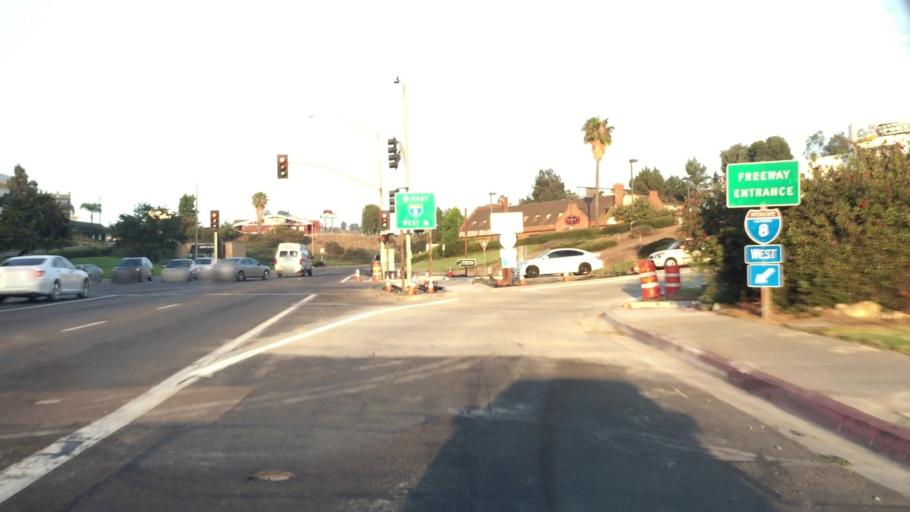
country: US
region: California
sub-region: San Diego County
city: La Mesa
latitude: 32.7760
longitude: -117.0139
